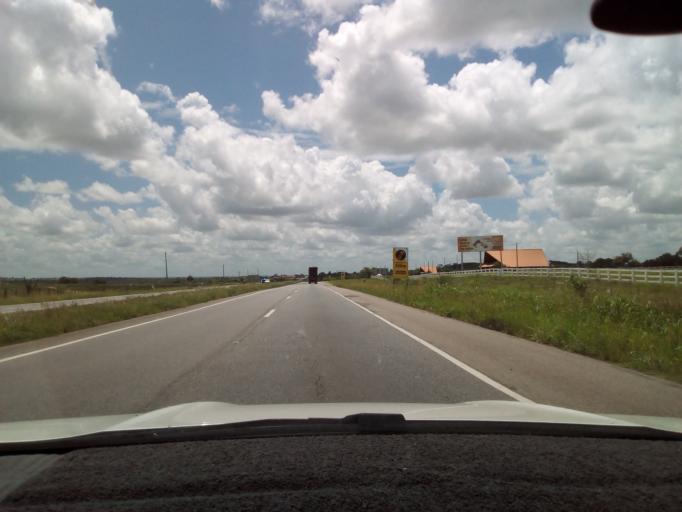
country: BR
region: Paraiba
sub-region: Gurinhem
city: Gurinhem
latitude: -7.1719
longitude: -35.3875
